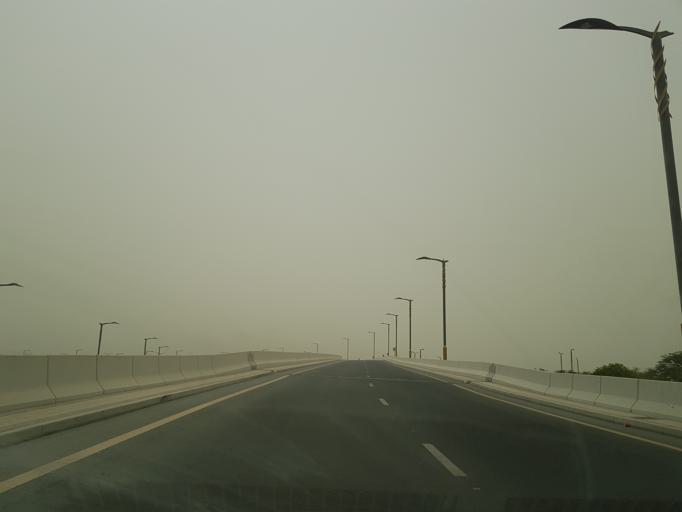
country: AE
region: Dubai
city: Dubai
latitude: 25.1561
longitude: 55.2927
